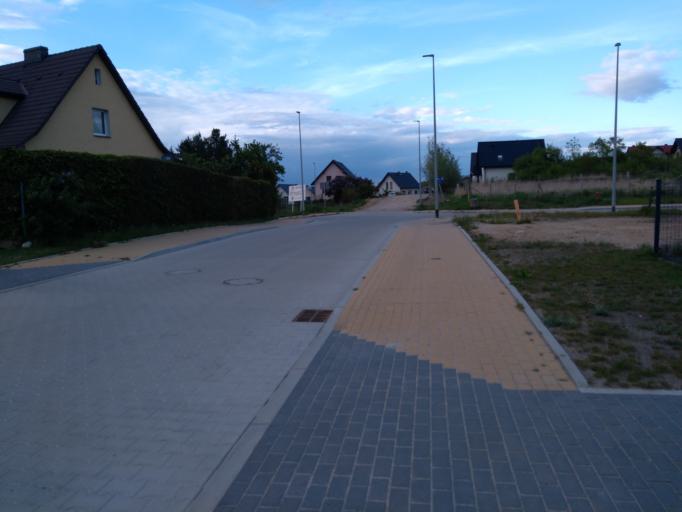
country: PL
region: West Pomeranian Voivodeship
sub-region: Powiat gryfinski
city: Gryfino
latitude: 53.2661
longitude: 14.5002
